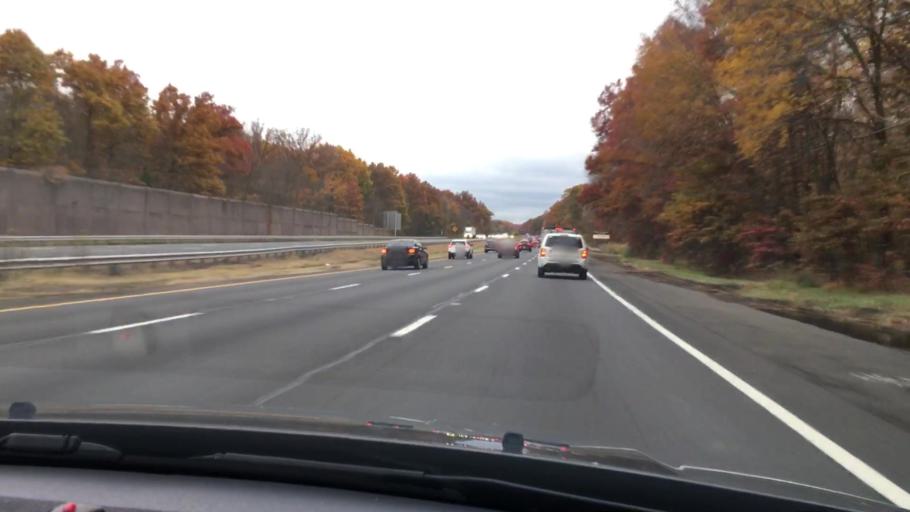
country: US
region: New Jersey
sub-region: Somerset County
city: Bernardsville
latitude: 40.6843
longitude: -74.5893
